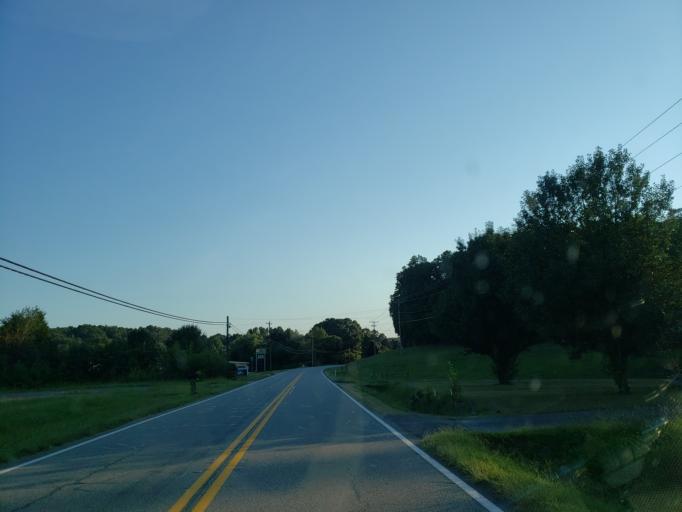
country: US
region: Georgia
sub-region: Gordon County
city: Calhoun
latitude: 34.5382
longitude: -84.9229
